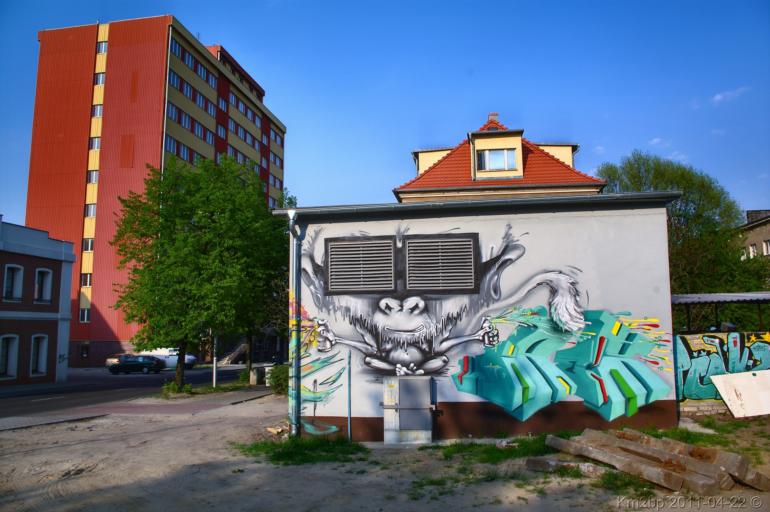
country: PL
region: Lubusz
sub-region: Zielona Gora
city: Zielona Gora
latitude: 51.9315
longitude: 15.5027
